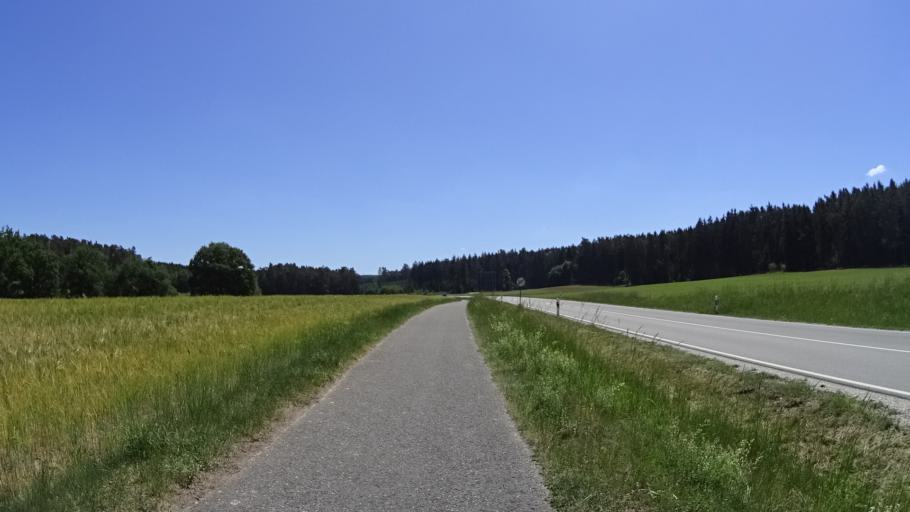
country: DE
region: Bavaria
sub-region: Regierungsbezirk Mittelfranken
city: Pleinfeld
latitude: 49.1007
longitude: 10.9571
